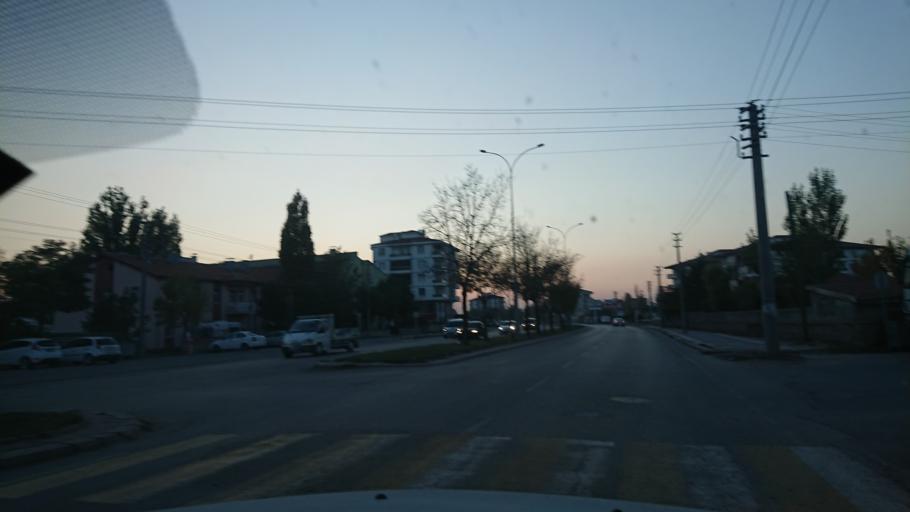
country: TR
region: Aksaray
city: Aksaray
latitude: 38.3604
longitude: 34.0028
